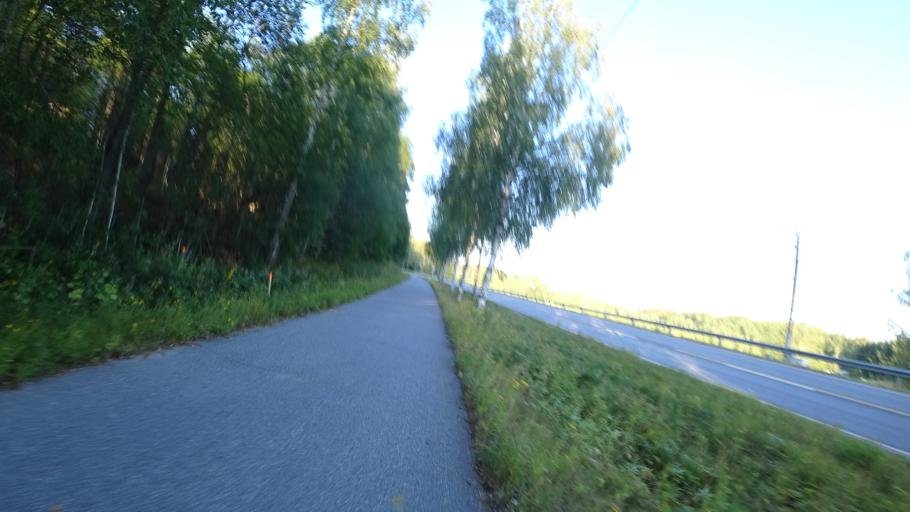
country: FI
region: Pirkanmaa
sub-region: Tampere
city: Nokia
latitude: 61.4674
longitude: 23.4428
